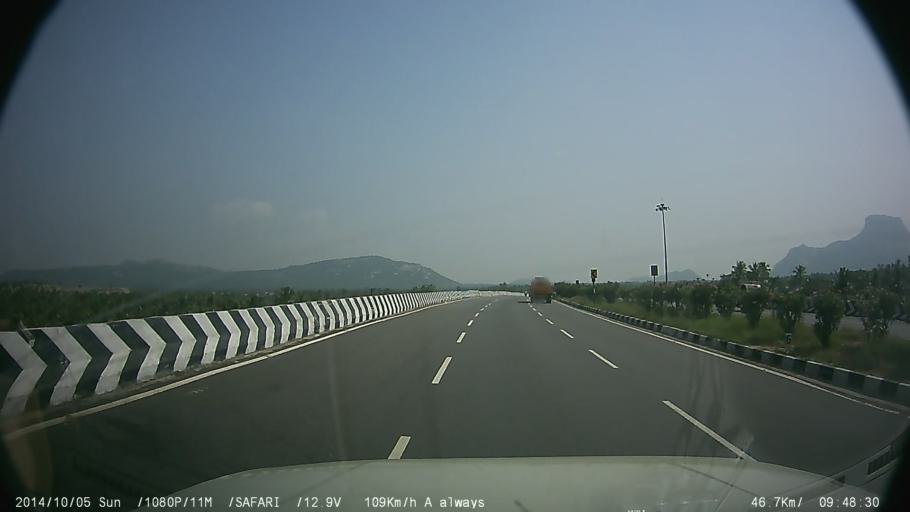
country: IN
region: Tamil Nadu
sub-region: Namakkal
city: Tiruchengode
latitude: 11.4664
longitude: 77.8227
